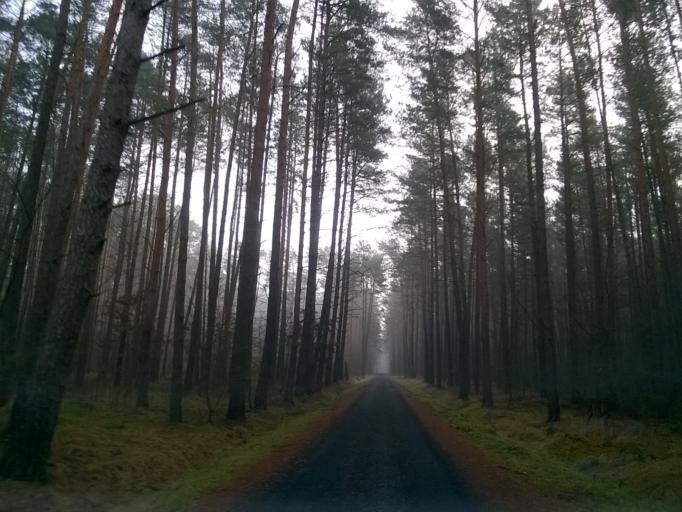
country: PL
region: Kujawsko-Pomorskie
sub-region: Powiat nakielski
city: Kcynia
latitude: 53.0512
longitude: 17.4655
